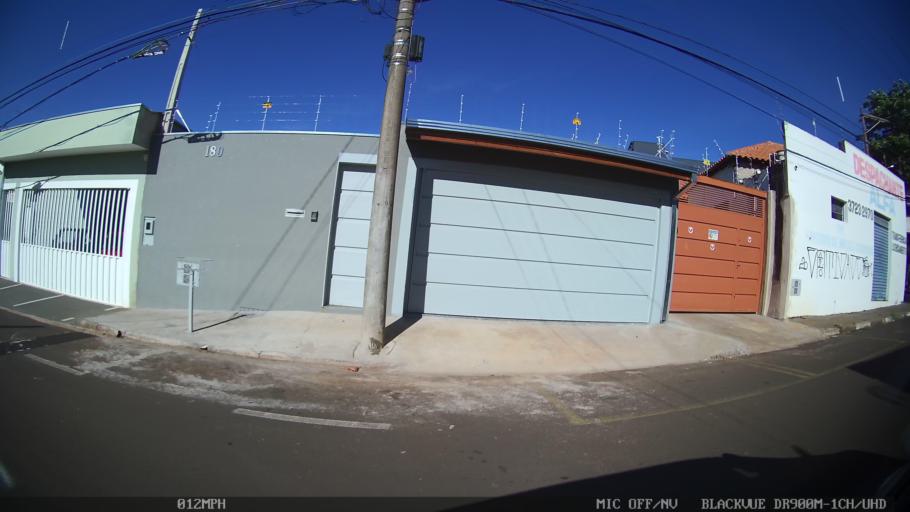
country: BR
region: Sao Paulo
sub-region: Franca
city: Franca
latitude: -20.5289
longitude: -47.4115
